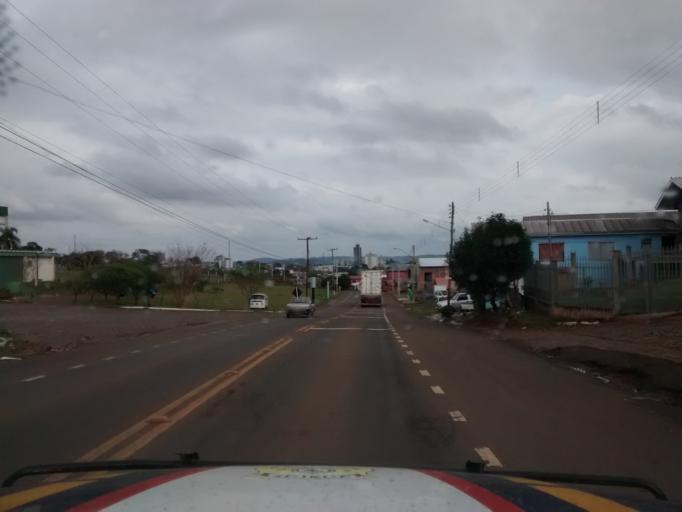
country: BR
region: Rio Grande do Sul
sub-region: Lagoa Vermelha
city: Lagoa Vermelha
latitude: -28.1969
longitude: -51.5248
